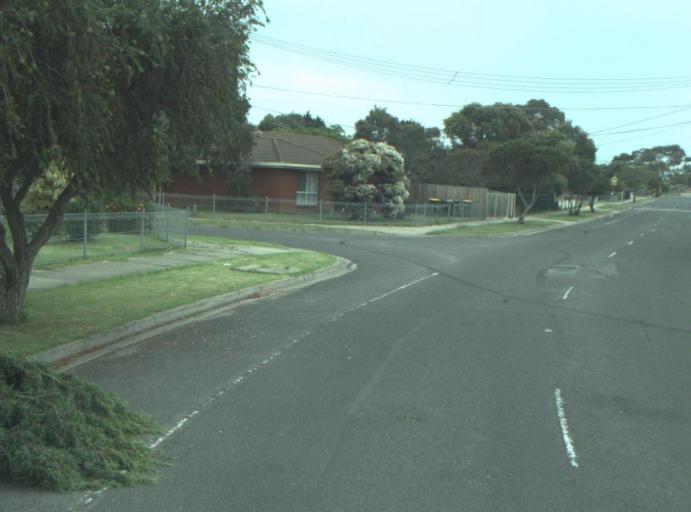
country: AU
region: Victoria
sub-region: Greater Geelong
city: Breakwater
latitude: -38.1787
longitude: 144.4003
